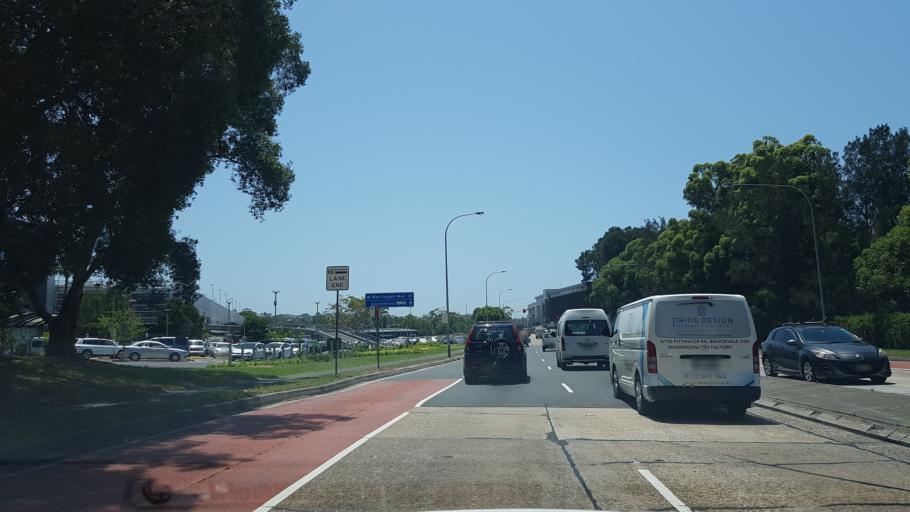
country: AU
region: New South Wales
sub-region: Warringah
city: North Manly
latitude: -33.7695
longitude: 151.2664
